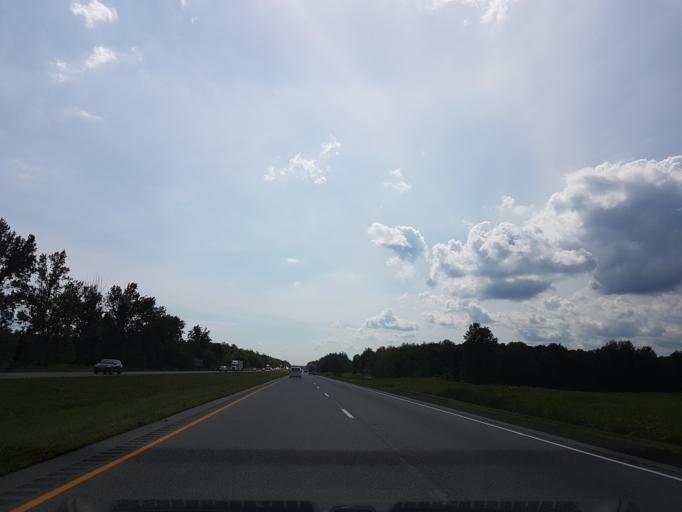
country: US
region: New York
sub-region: St. Lawrence County
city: Ogdensburg
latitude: 44.8010
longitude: -75.4210
